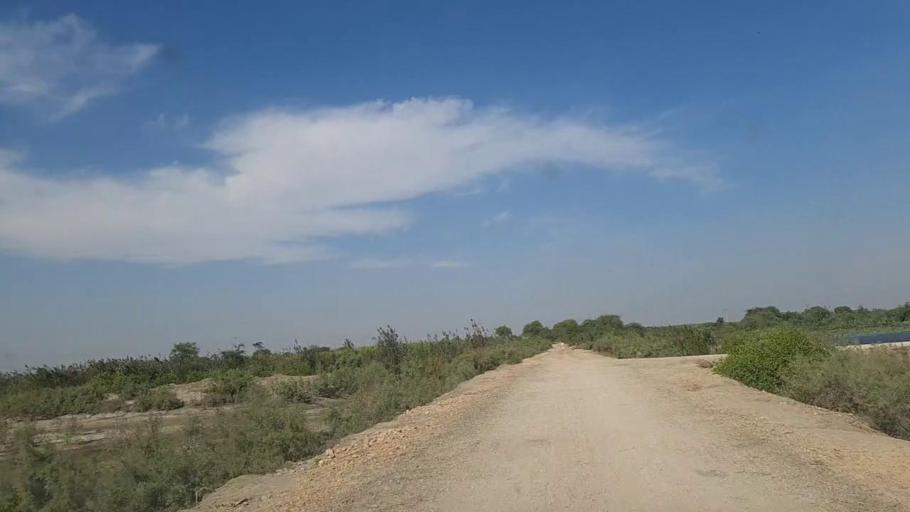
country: PK
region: Sindh
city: Bulri
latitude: 24.8209
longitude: 68.2666
